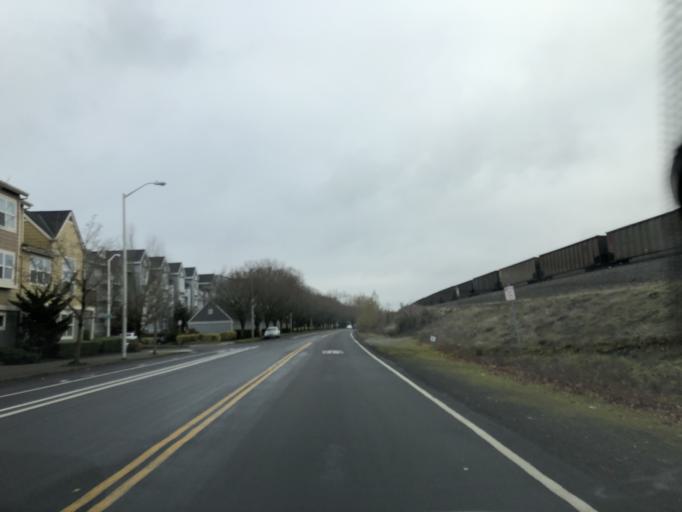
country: US
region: Washington
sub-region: Clark County
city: Vancouver
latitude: 45.6174
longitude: -122.6536
